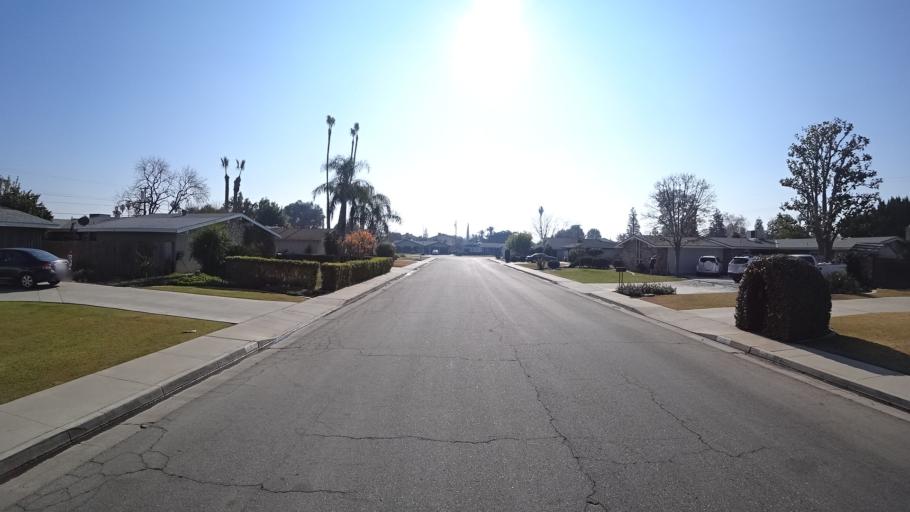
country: US
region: California
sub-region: Kern County
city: Greenacres
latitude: 35.3561
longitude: -119.0712
